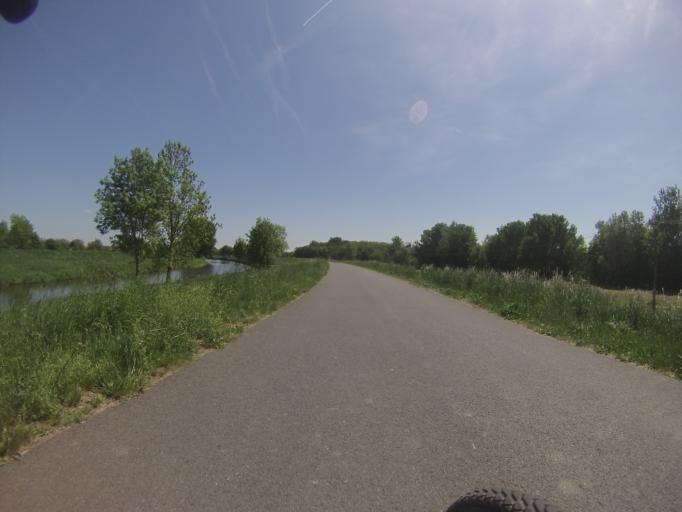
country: CZ
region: South Moravian
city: Vranovice
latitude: 48.9265
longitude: 16.5732
